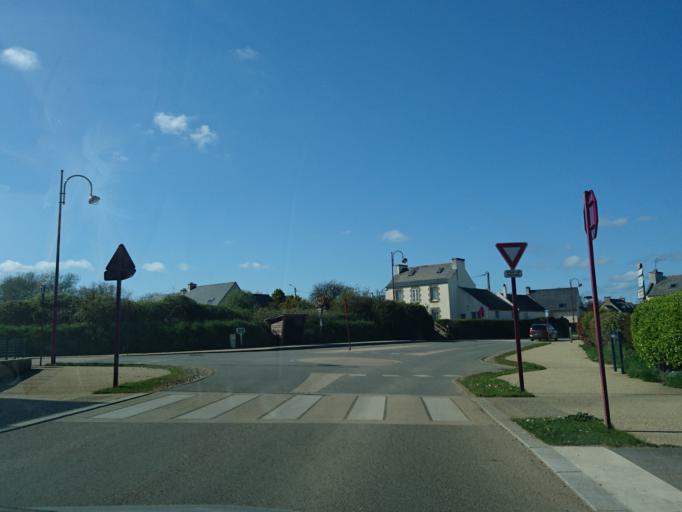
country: FR
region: Brittany
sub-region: Departement du Finistere
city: Lanrivoare
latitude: 48.4740
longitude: -4.6402
